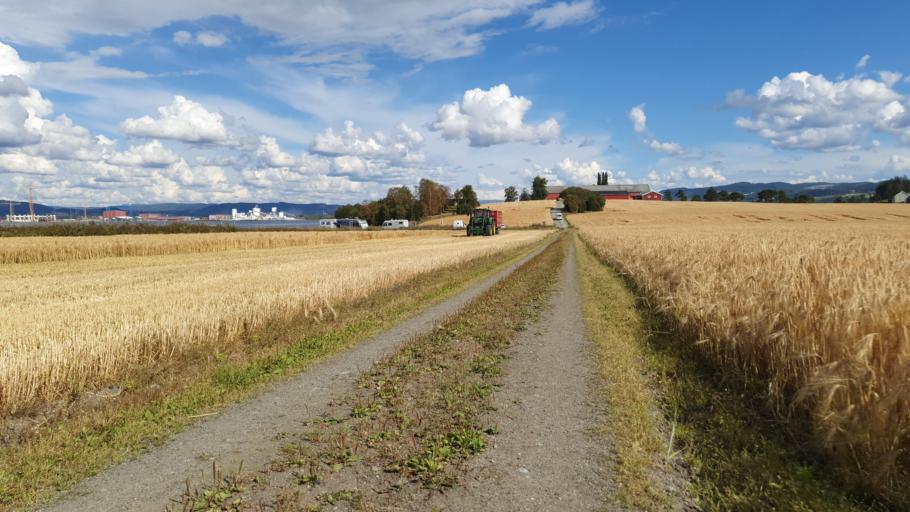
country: NO
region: Nord-Trondelag
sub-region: Levanger
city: Levanger
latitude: 63.7776
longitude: 11.3885
